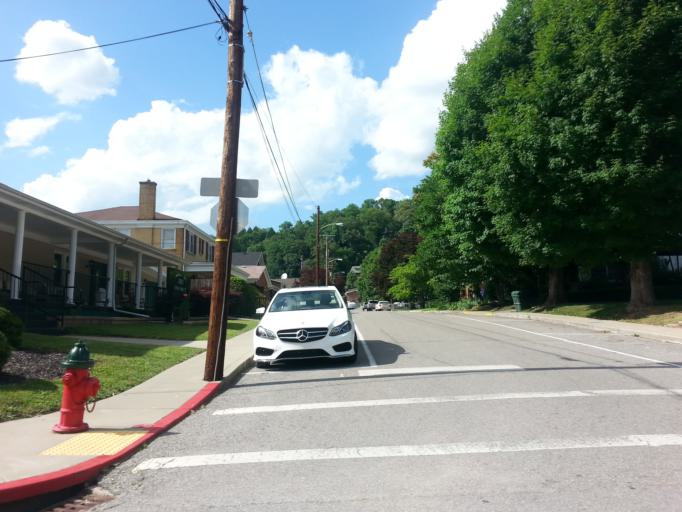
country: US
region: Kentucky
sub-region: Harlan County
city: Harlan
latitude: 36.8458
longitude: -83.3201
